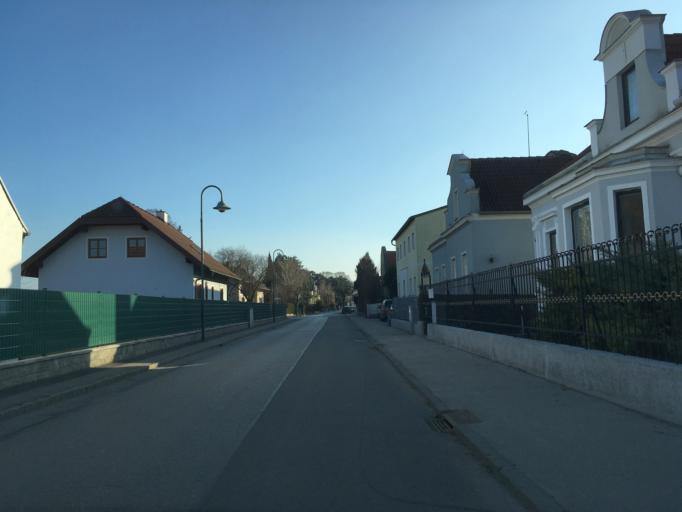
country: AT
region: Lower Austria
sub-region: Politischer Bezirk Tulln
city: Konigstetten
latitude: 48.3312
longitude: 16.1209
